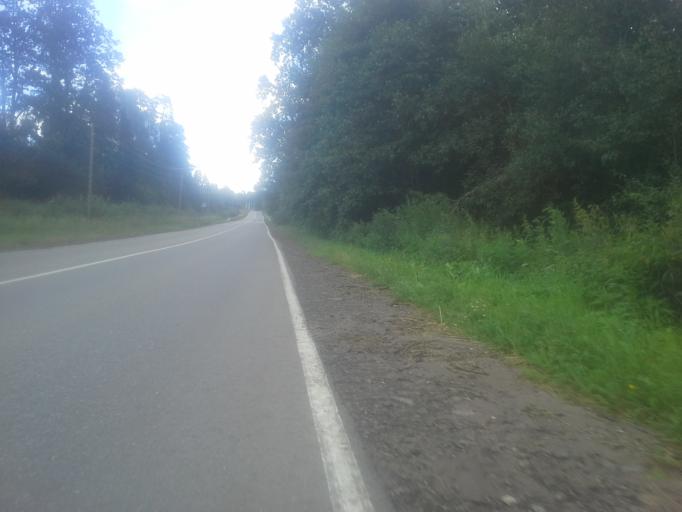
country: RU
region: Moskovskaya
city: Karinskoye
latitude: 55.6666
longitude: 36.6493
